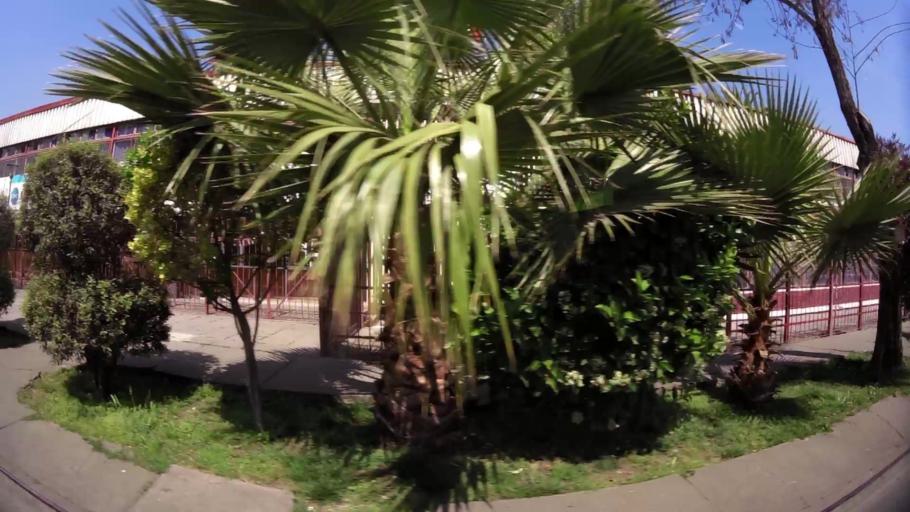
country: CL
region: Santiago Metropolitan
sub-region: Provincia de Santiago
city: Santiago
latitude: -33.4566
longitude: -70.6772
